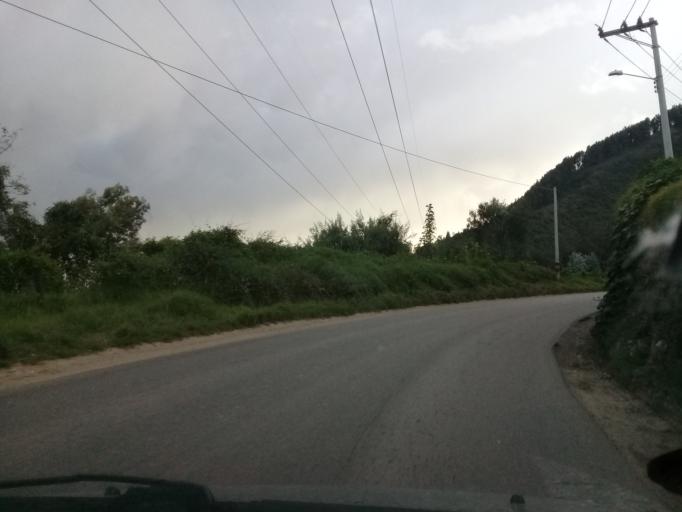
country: CO
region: Cundinamarca
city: Tabio
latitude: 4.9240
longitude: -74.0634
